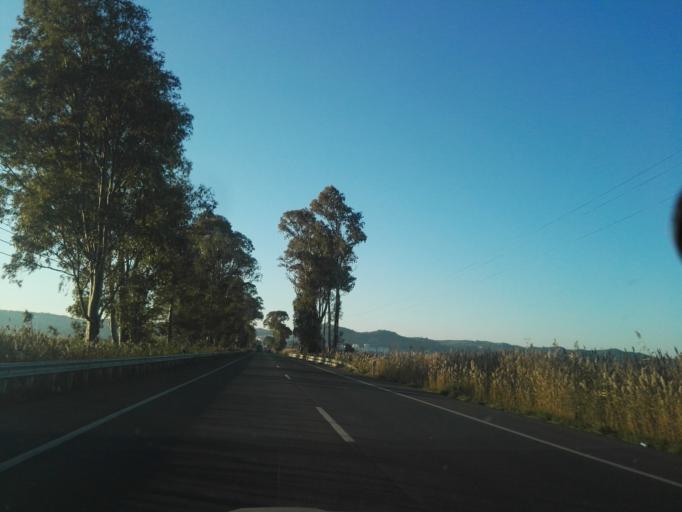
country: PT
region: Lisbon
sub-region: Vila Franca de Xira
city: Vila Franca de Xira
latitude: 38.9448
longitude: -8.9536
